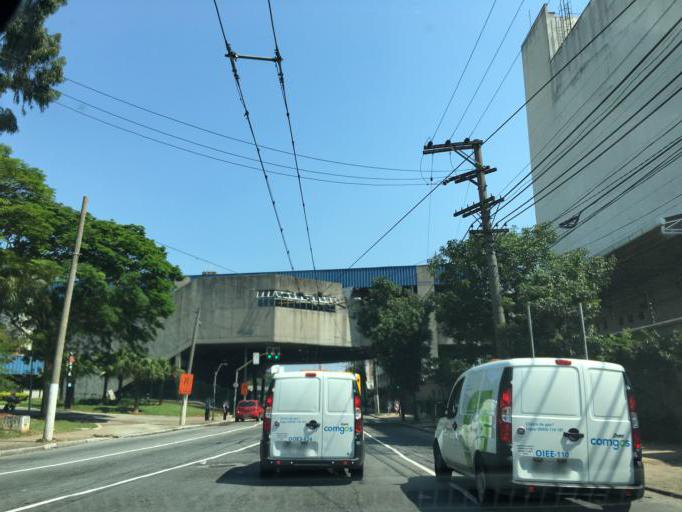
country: BR
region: Sao Paulo
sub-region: Sao Paulo
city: Sao Paulo
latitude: -23.5504
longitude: -46.6251
